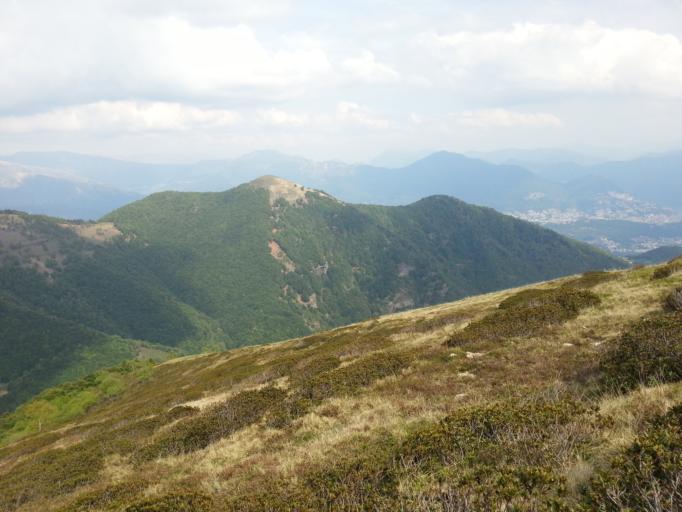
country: IT
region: Lombardy
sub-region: Provincia di Varese
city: Curiglia
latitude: 46.0660
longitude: 8.8627
